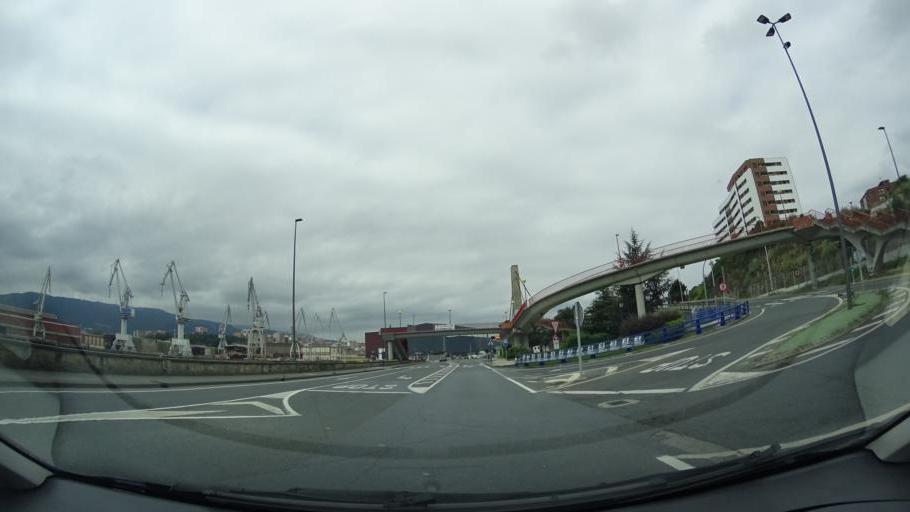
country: ES
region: Basque Country
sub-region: Bizkaia
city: Leioa
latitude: 43.3125
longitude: -2.9836
